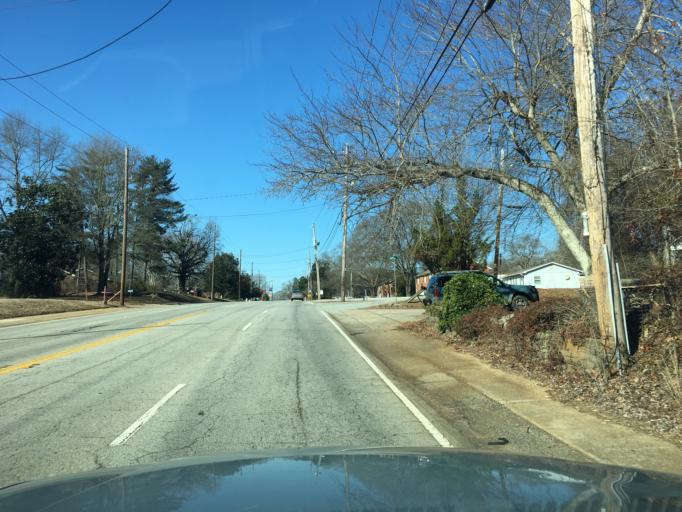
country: US
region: South Carolina
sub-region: Greenville County
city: Sans Souci
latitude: 34.8936
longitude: -82.4270
